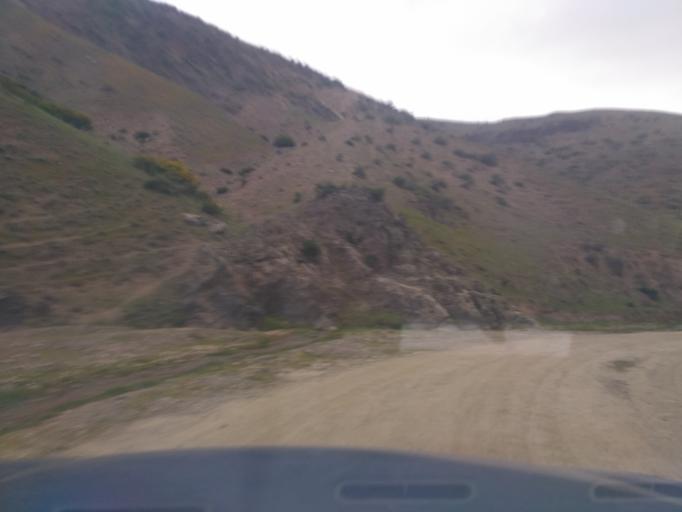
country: UZ
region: Jizzax
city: Zomin
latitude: 39.8548
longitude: 68.3895
